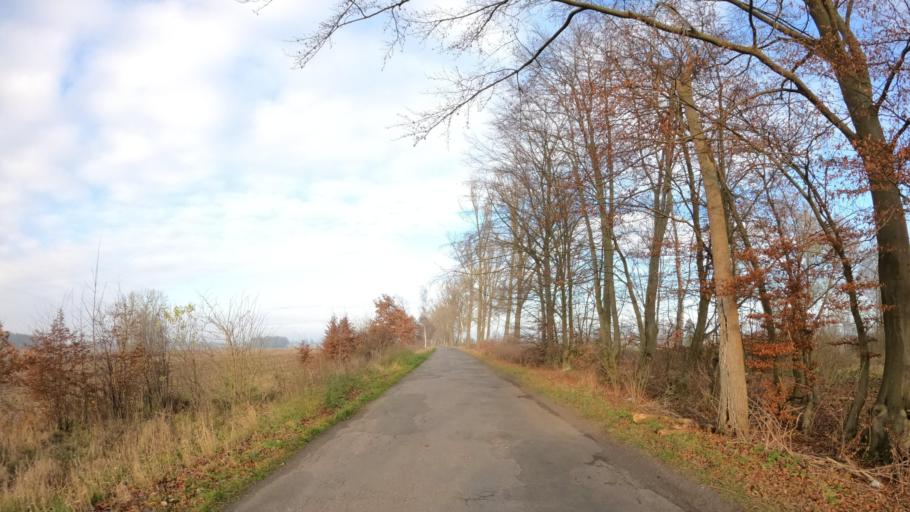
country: PL
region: West Pomeranian Voivodeship
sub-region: Powiat goleniowski
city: Maszewo
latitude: 53.5666
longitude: 15.0907
